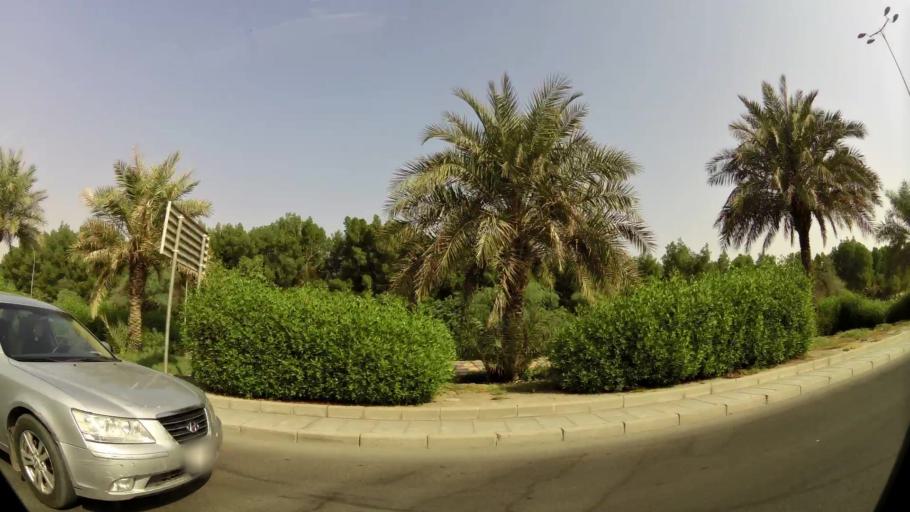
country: KW
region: Al Asimah
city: Ar Rabiyah
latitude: 29.2746
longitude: 47.8657
